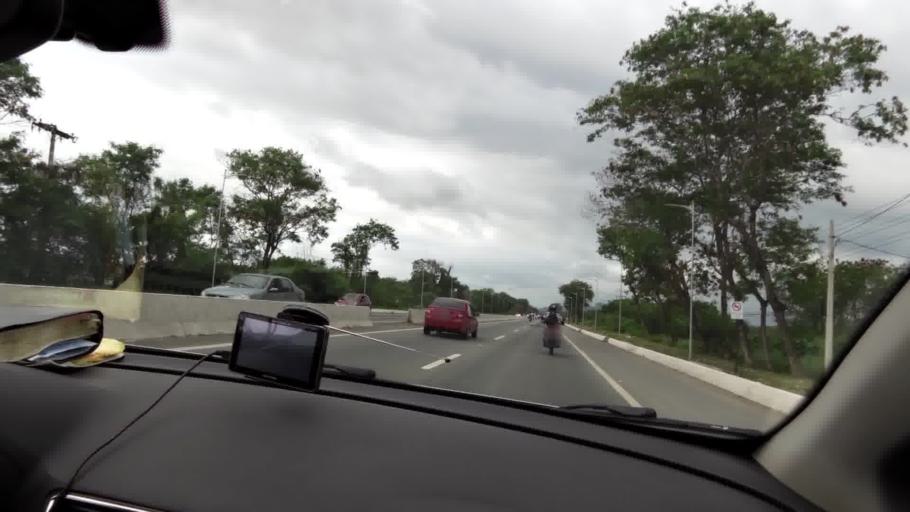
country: BR
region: Espirito Santo
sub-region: Vila Velha
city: Vila Velha
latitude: -20.2428
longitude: -40.2814
